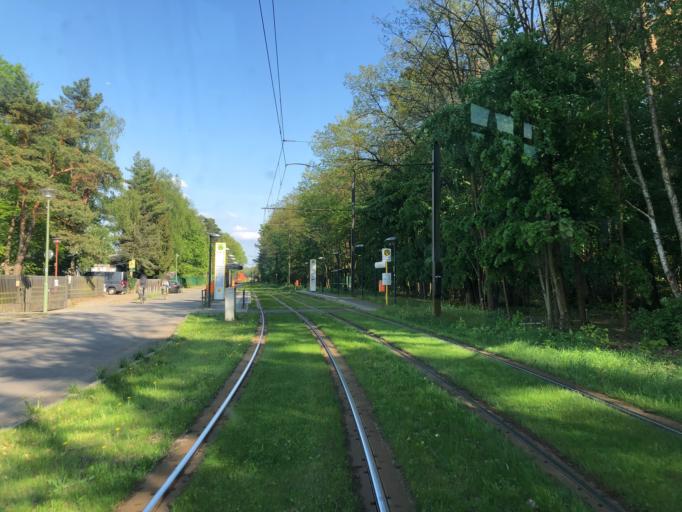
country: DE
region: Berlin
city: Grunau
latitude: 52.4087
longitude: 13.6037
